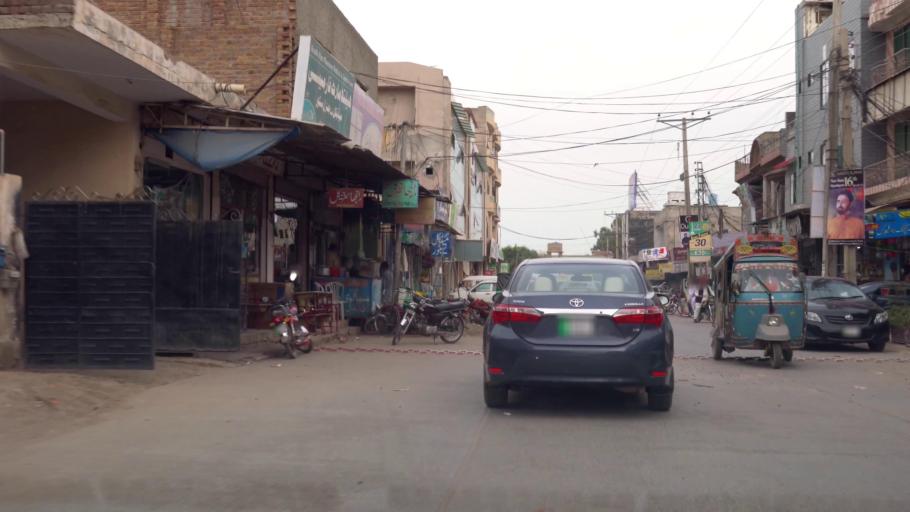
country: PK
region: Punjab
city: Sargodha
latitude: 32.0796
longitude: 72.6801
